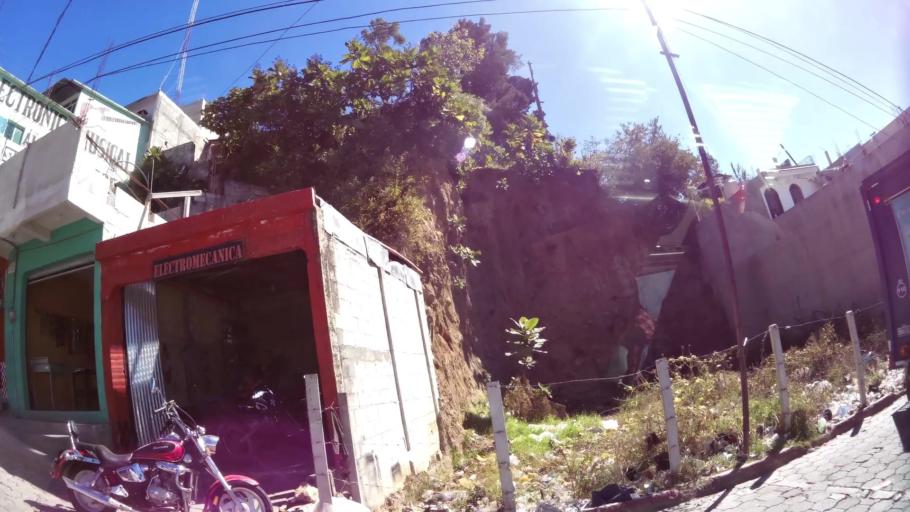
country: GT
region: Solola
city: Solola
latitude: 14.7743
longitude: -91.1836
